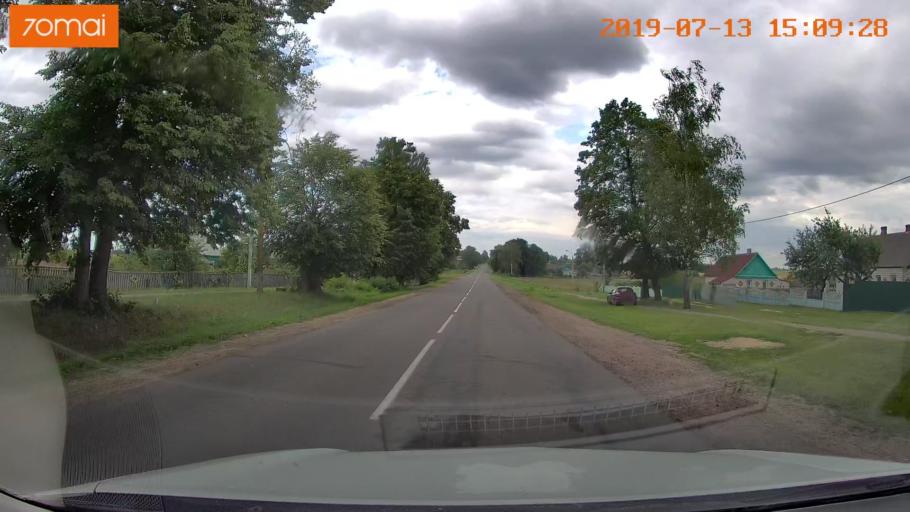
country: BY
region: Mogilev
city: Hlusha
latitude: 53.1729
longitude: 28.7626
